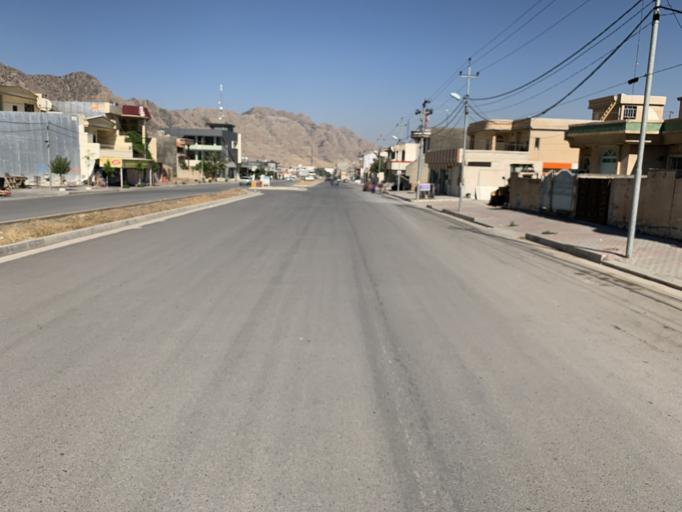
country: IQ
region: As Sulaymaniyah
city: Raniye
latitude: 36.2583
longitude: 44.8688
